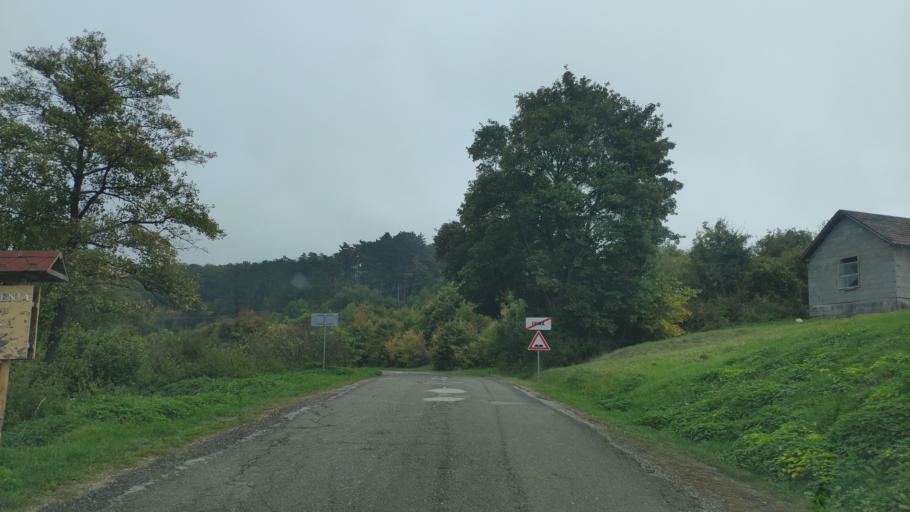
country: SK
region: Kosicky
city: Kosice
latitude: 48.8574
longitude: 21.4311
